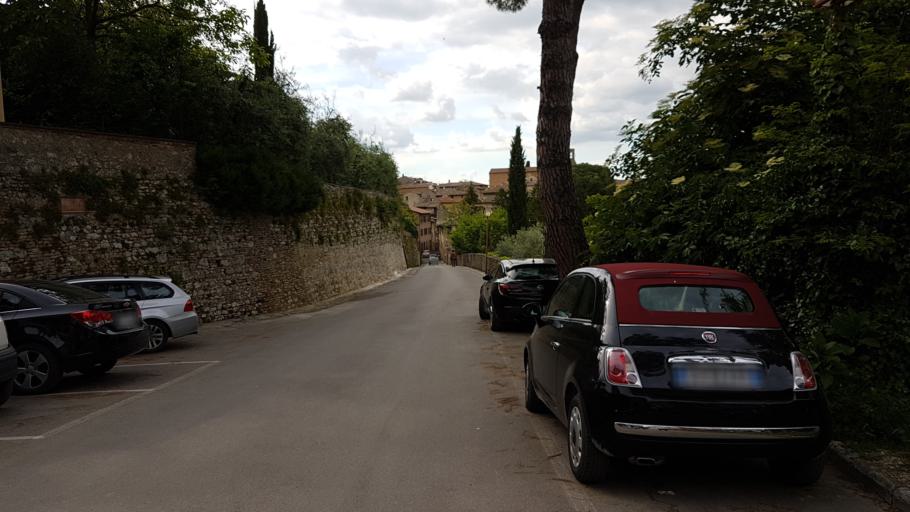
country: IT
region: Tuscany
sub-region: Provincia di Siena
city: San Gimignano
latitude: 43.4683
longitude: 11.0447
